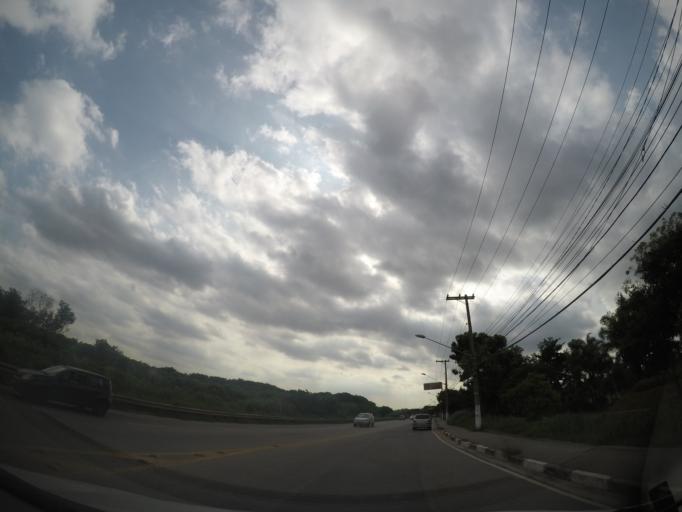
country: BR
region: Sao Paulo
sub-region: Guarulhos
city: Guarulhos
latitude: -23.4171
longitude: -46.4721
